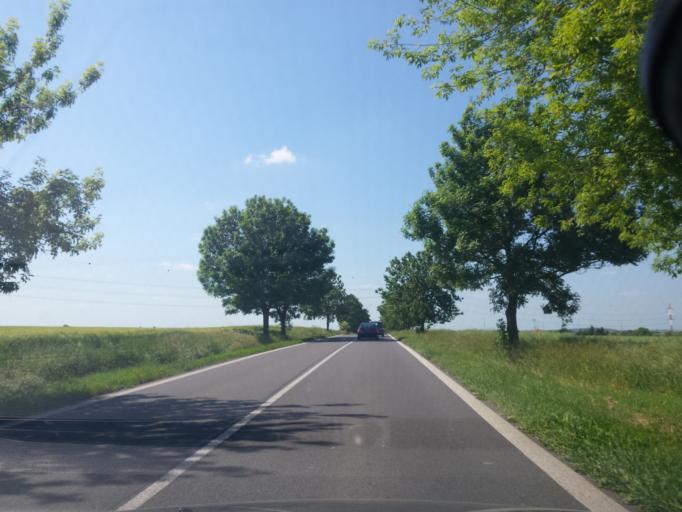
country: CZ
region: Central Bohemia
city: Horomerice
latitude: 50.1197
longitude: 14.3576
